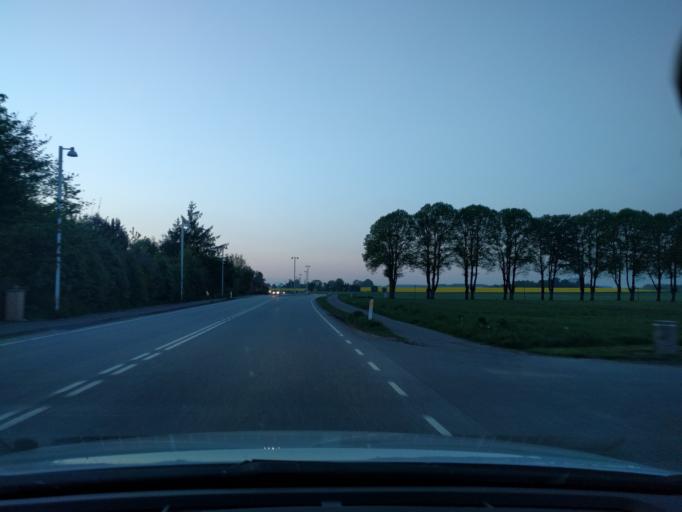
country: DK
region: Zealand
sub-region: Guldborgsund Kommune
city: Norre Alslev
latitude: 54.8478
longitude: 11.8581
